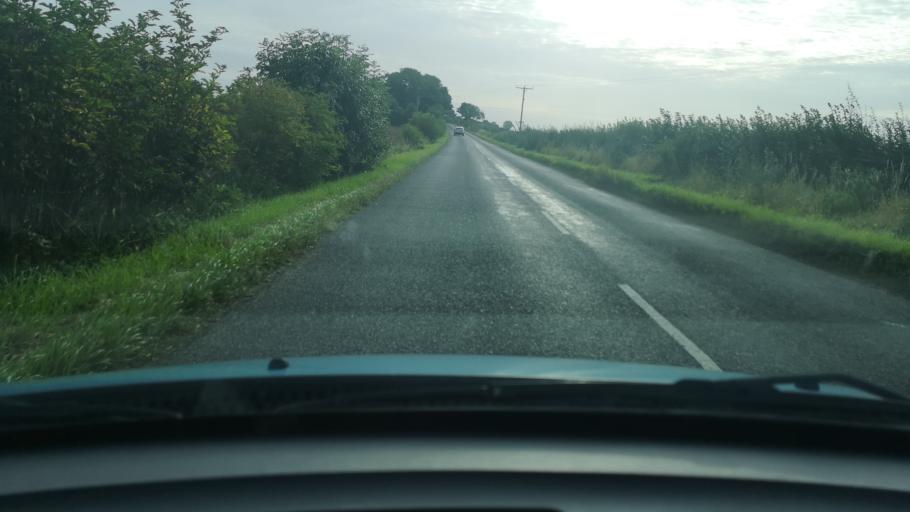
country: GB
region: England
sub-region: Doncaster
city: Norton
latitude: 53.6183
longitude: -1.2181
